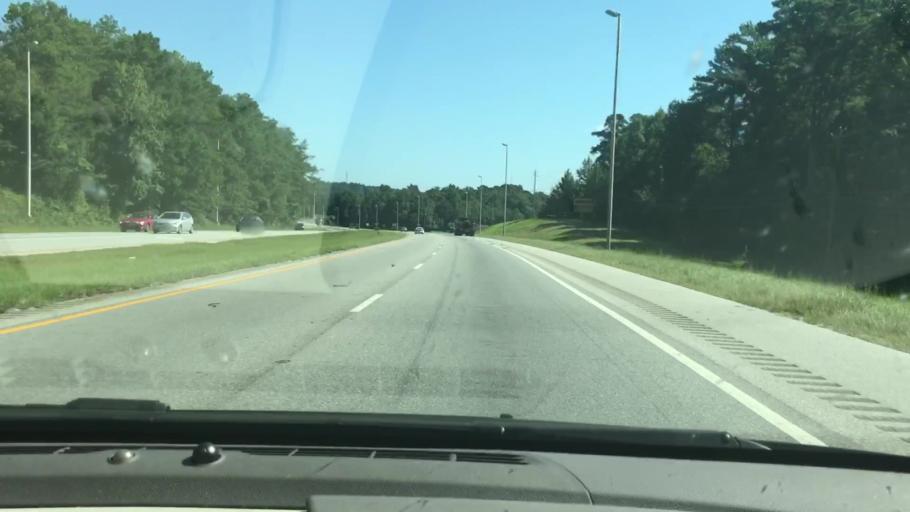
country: US
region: Alabama
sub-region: Russell County
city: Phenix City
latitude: 32.4313
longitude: -85.0283
